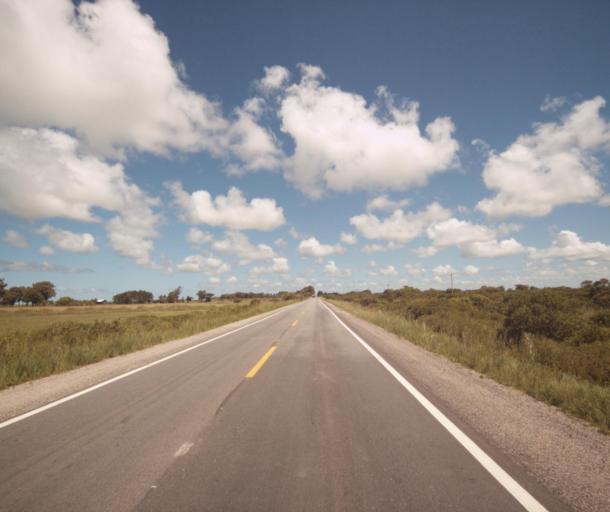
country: UY
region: Cerro Largo
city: Rio Branco
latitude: -32.9902
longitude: -52.8141
